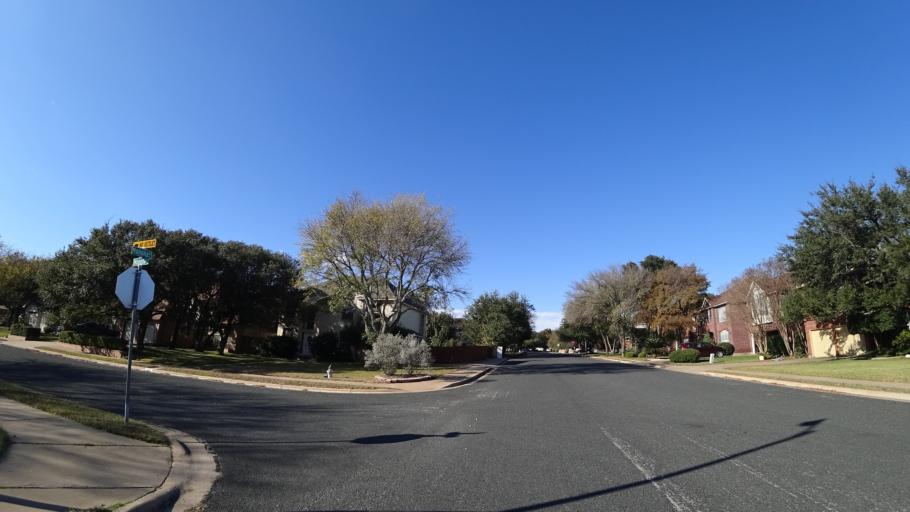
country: US
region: Texas
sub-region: Williamson County
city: Brushy Creek
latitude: 30.4893
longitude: -97.7378
